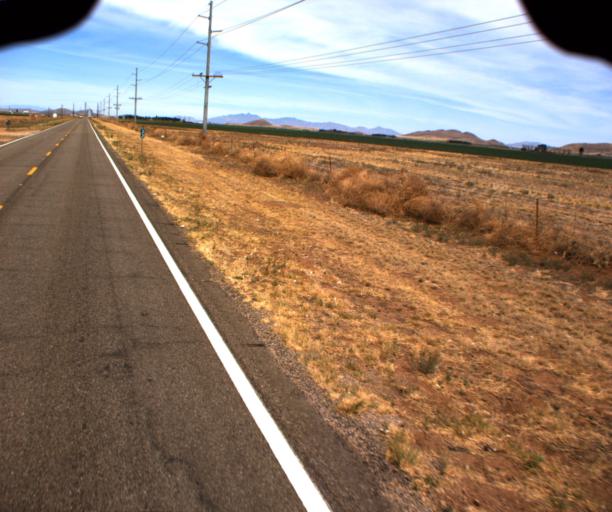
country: US
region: Arizona
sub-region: Cochise County
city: Tombstone
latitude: 31.8098
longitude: -109.6942
